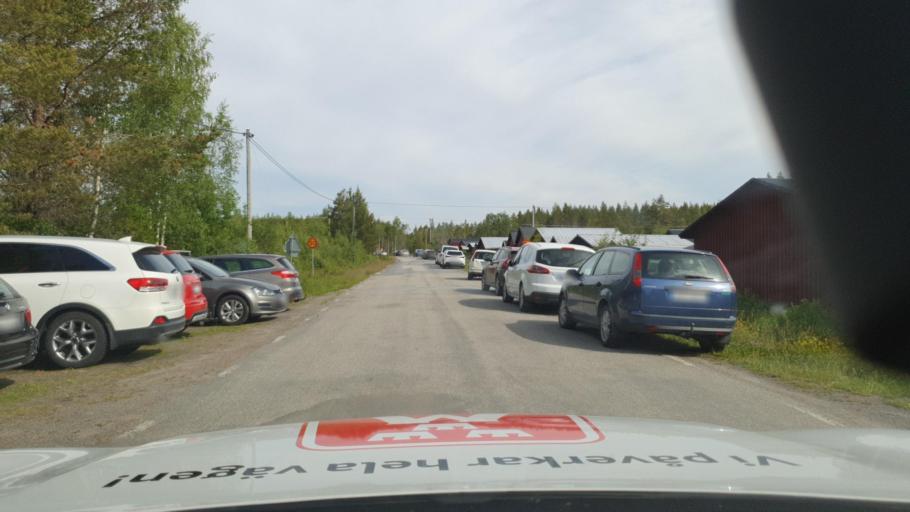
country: SE
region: Vaesterbotten
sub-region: Umea Kommun
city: Saevar
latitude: 63.8641
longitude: 20.7372
